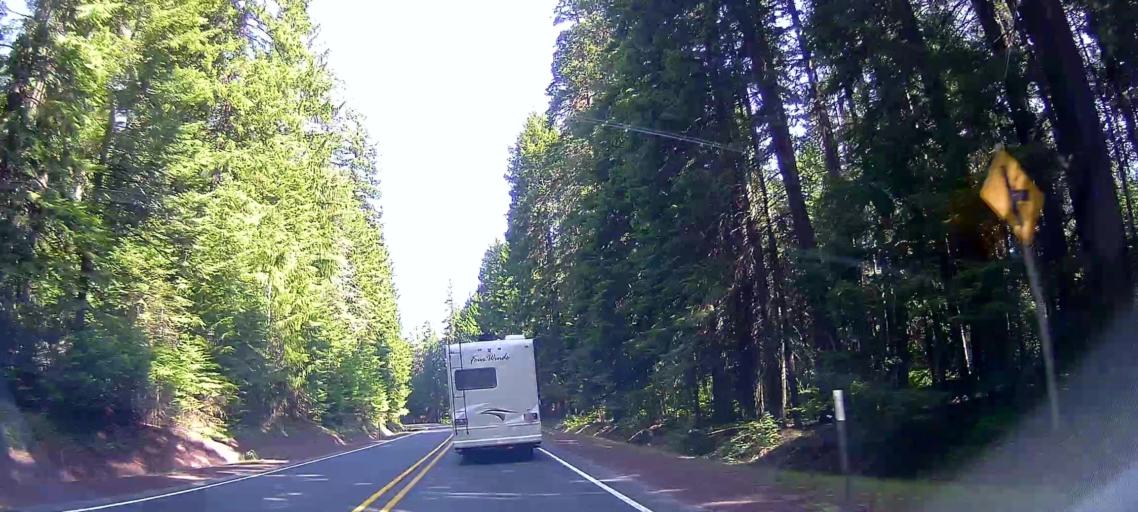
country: US
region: Oregon
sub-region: Jefferson County
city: Warm Springs
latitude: 45.0857
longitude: -121.5443
